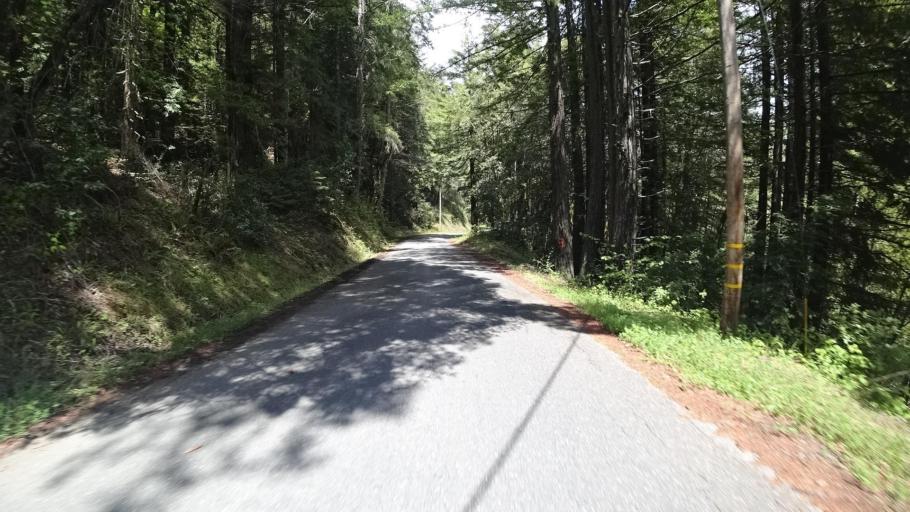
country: US
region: California
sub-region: Humboldt County
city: Blue Lake
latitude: 40.8452
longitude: -123.8974
